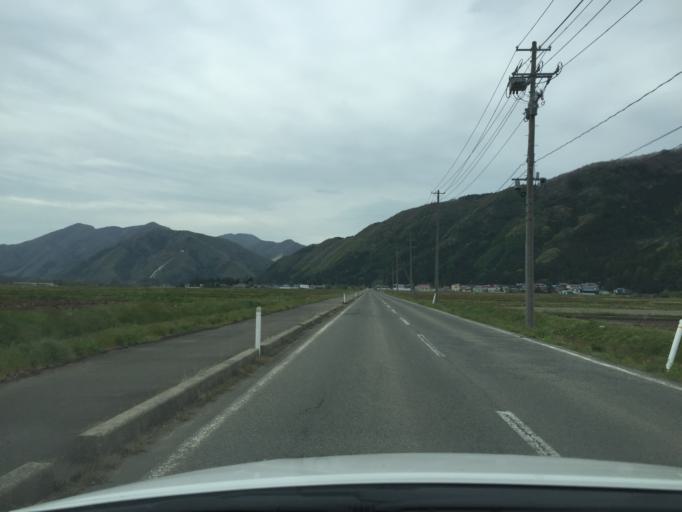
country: JP
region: Fukushima
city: Inawashiro
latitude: 37.5851
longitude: 140.1383
